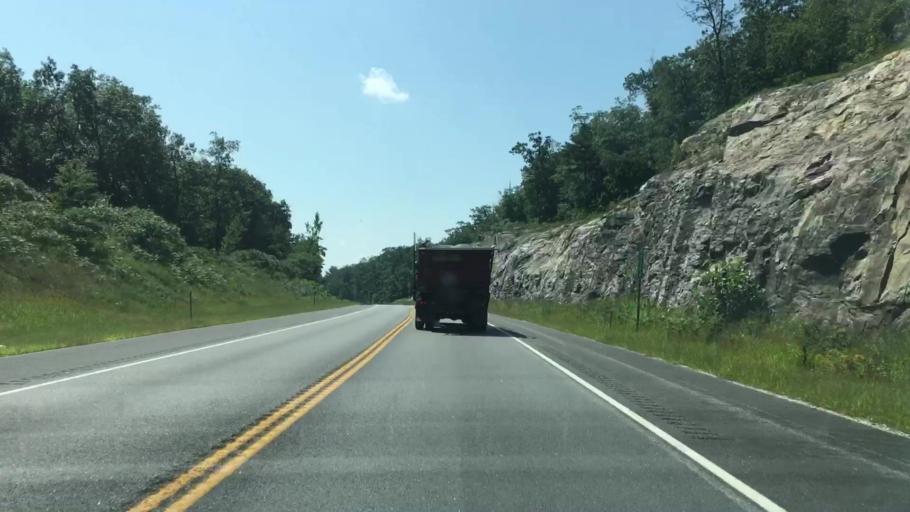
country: US
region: New Hampshire
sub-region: Rockingham County
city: Salem
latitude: 42.8305
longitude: -71.2384
